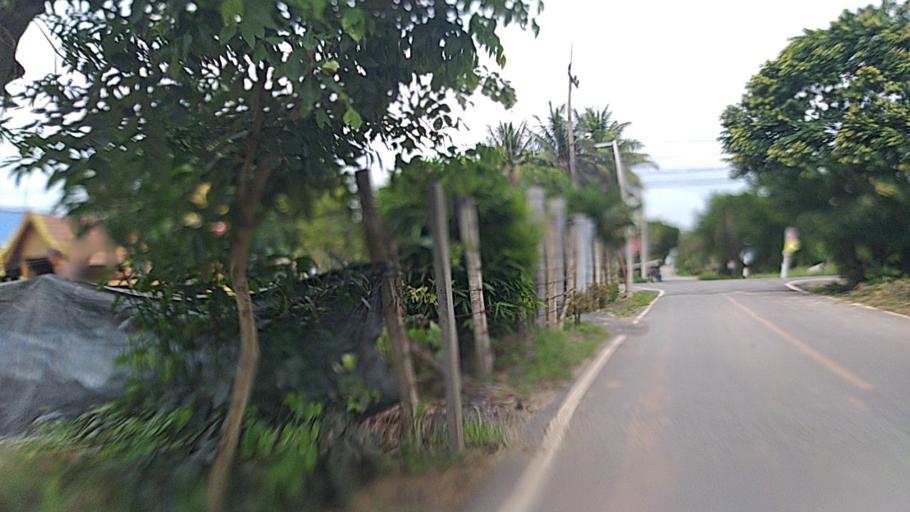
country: TH
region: Pathum Thani
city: Ban Lam Luk Ka
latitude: 14.0342
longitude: 100.8704
